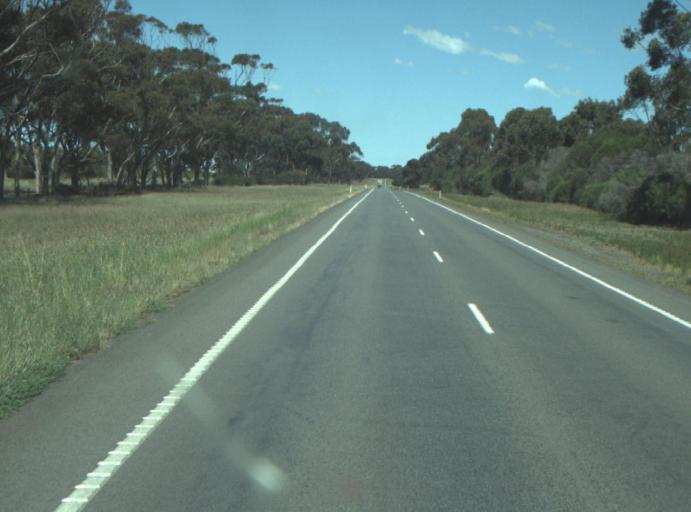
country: AU
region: Victoria
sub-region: Greater Geelong
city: Lara
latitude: -37.9452
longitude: 144.3559
